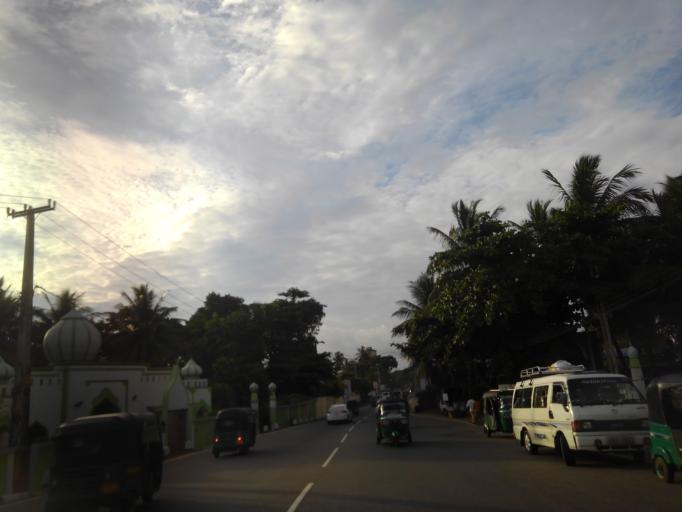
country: LK
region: Southern
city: Galle
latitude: 6.0355
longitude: 80.2318
